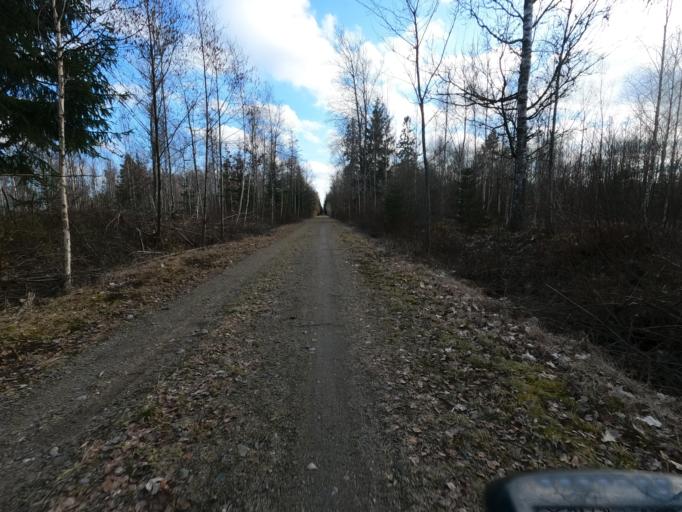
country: SE
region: Kronoberg
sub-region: Alvesta Kommun
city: Vislanda
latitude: 56.6547
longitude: 14.6185
